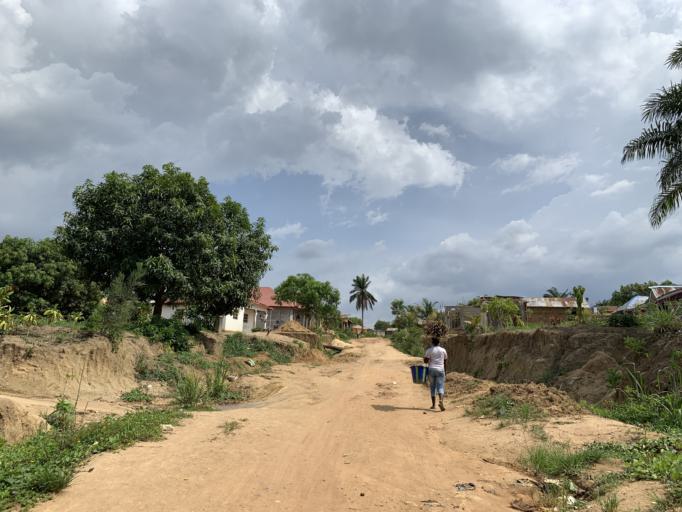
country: SL
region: Western Area
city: Waterloo
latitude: 8.3499
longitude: -13.0495
